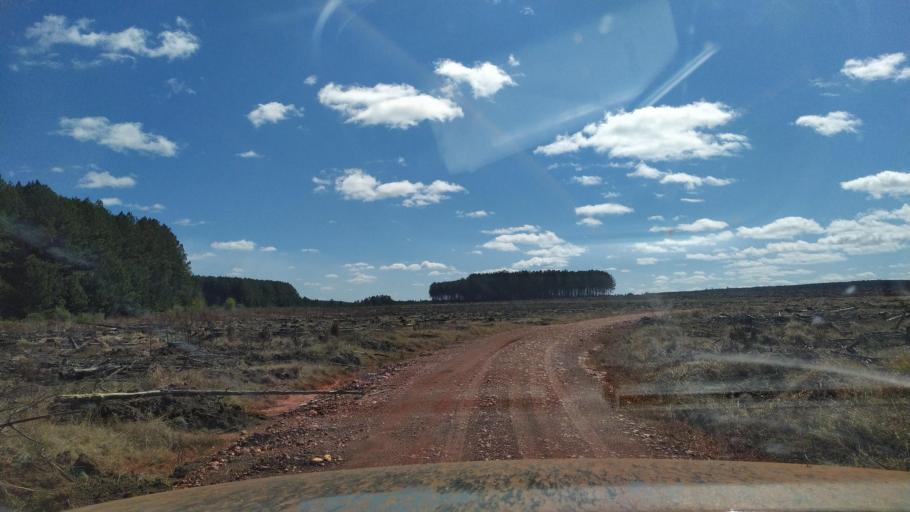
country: AR
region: Corrientes
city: Gobernador Ingeniero Valentin Virasoro
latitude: -28.2982
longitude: -56.0530
